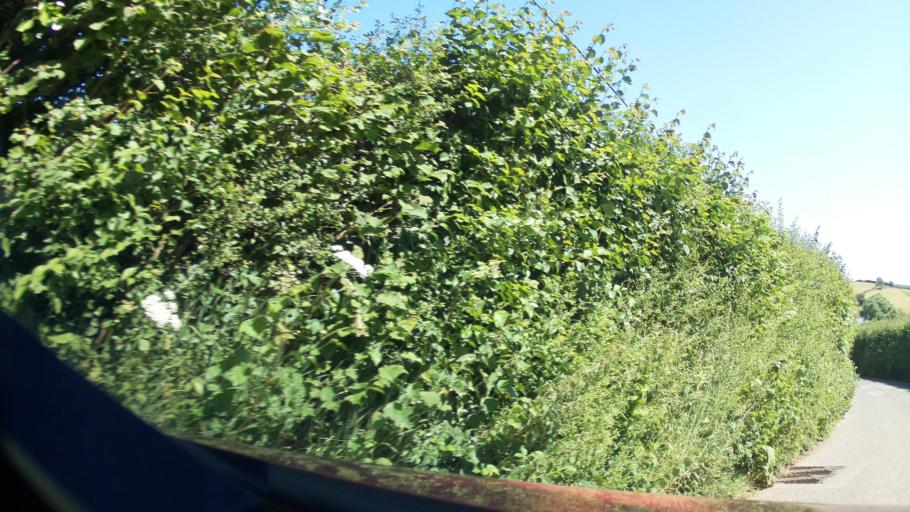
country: GB
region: England
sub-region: Devon
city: Marldon
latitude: 50.4811
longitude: -3.6074
